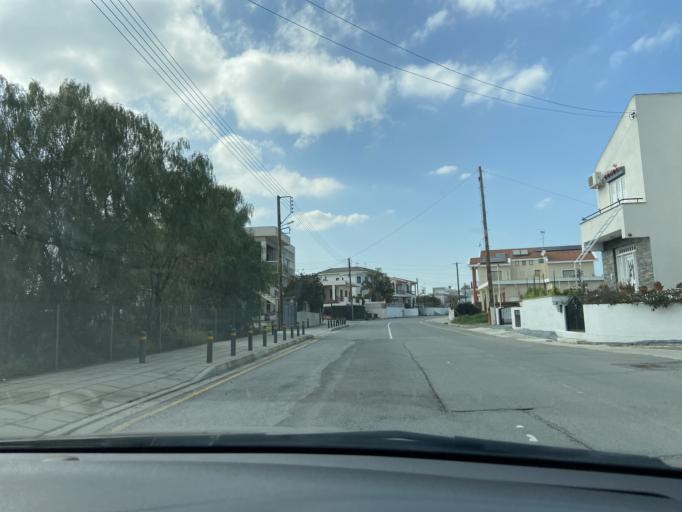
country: CY
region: Lefkosia
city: Alampra
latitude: 35.0201
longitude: 33.3892
